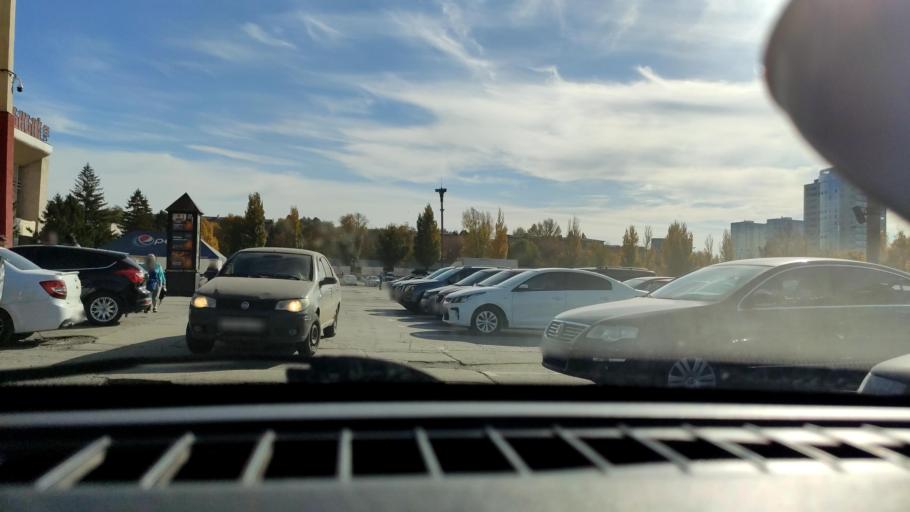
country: RU
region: Samara
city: Samara
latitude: 53.2170
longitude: 50.1882
